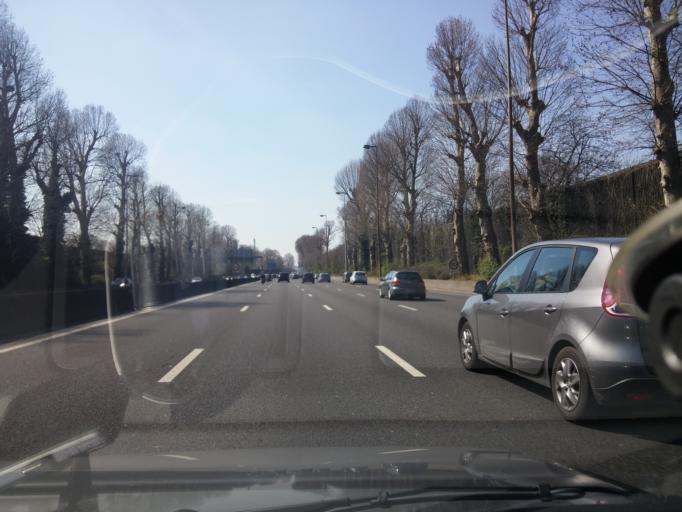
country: FR
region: Ile-de-France
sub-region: Departement du Val-de-Marne
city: Saint-Maurice
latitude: 48.8174
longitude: 2.4320
